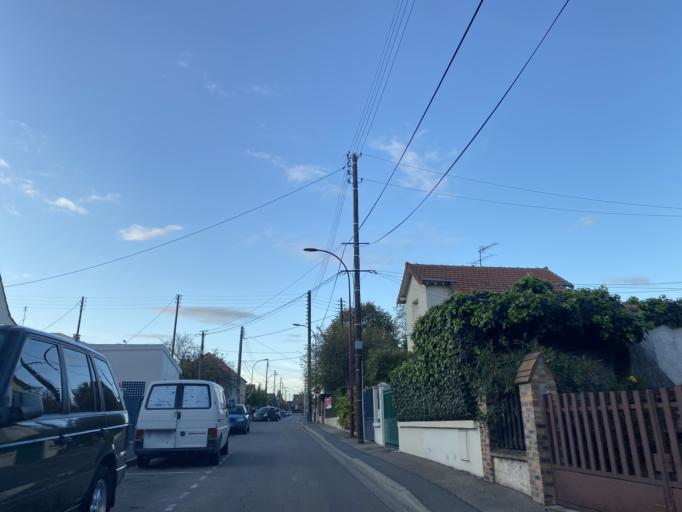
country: FR
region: Ile-de-France
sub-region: Departement du Val-d'Oise
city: Bezons
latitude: 48.9272
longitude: 2.2044
